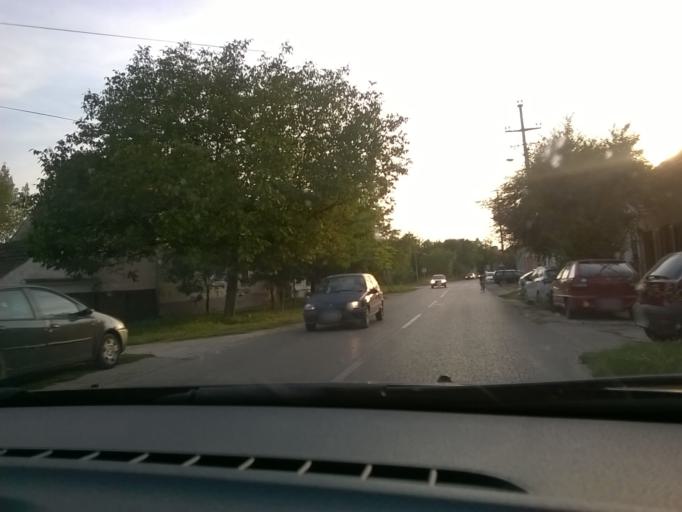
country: RS
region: Autonomna Pokrajina Vojvodina
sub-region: Juznobanatski Okrug
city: Vrsac
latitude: 45.1091
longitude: 21.2897
